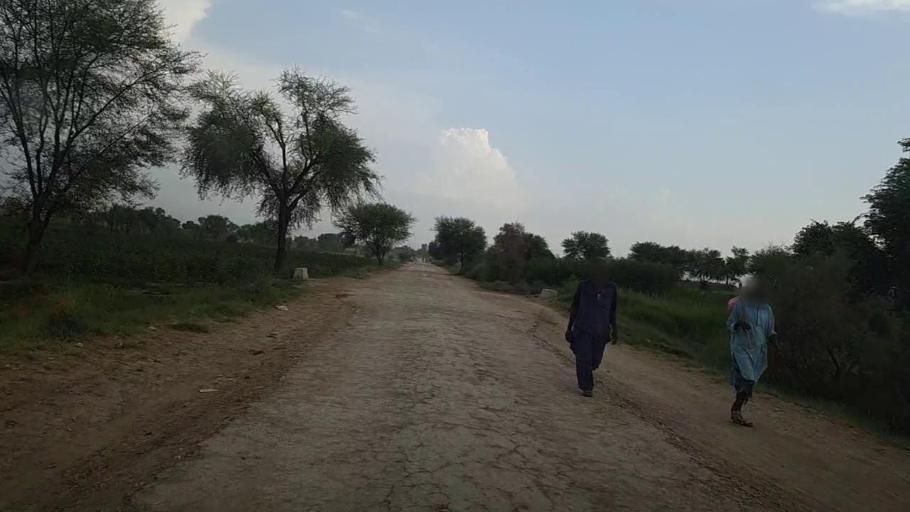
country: PK
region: Sindh
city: Khanpur
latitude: 27.8586
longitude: 69.4868
